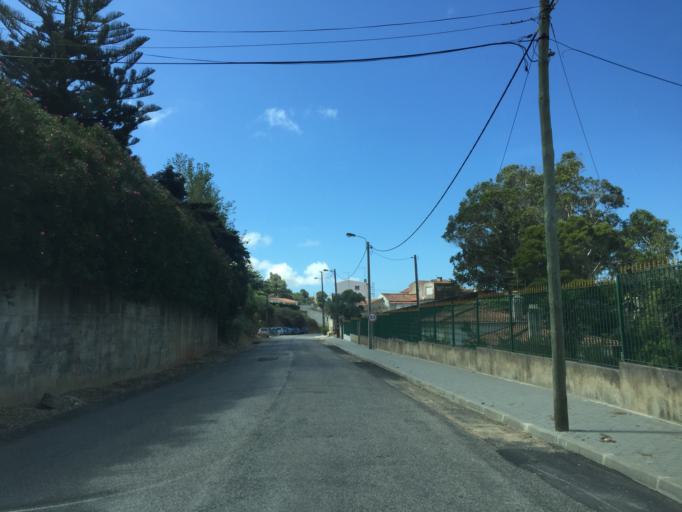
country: PT
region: Lisbon
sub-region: Sintra
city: Colares
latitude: 38.7581
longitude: -9.4458
